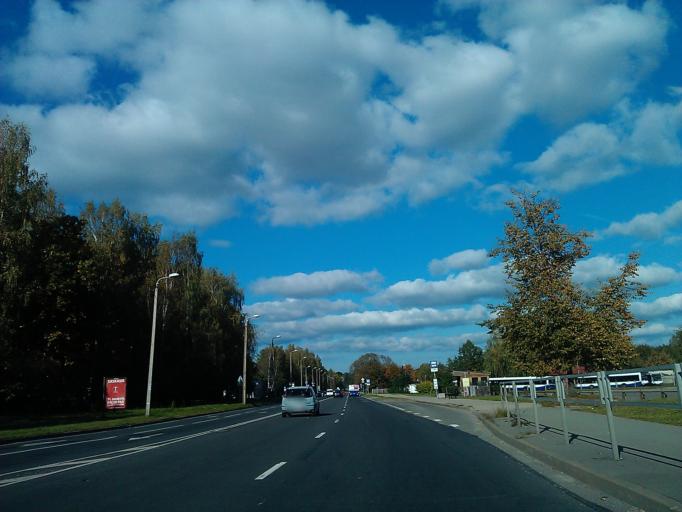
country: LV
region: Riga
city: Bergi
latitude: 56.9760
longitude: 24.2546
